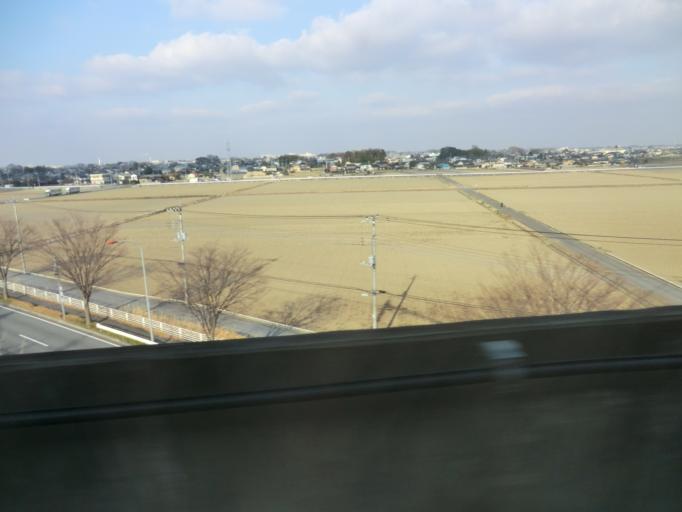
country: JP
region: Saitama
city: Fukiage-fujimi
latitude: 36.0956
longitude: 139.4880
